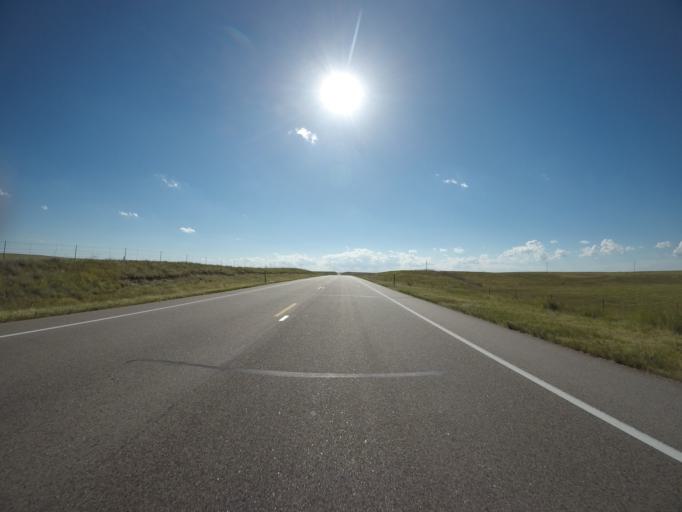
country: US
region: Colorado
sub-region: Logan County
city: Sterling
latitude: 40.6109
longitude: -103.5481
